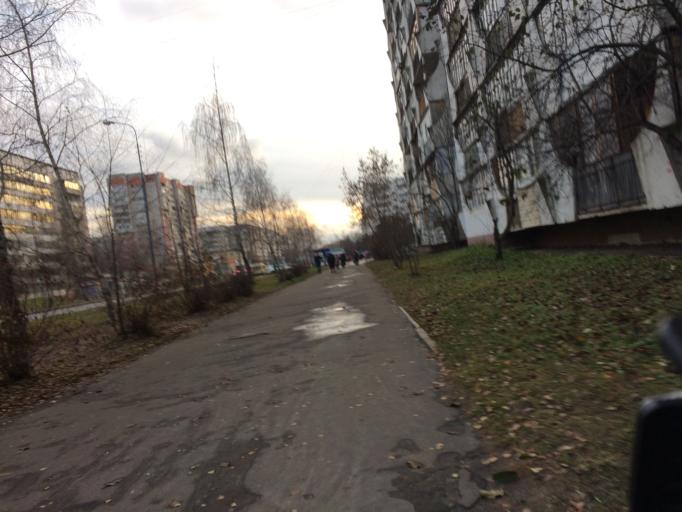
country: RU
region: Mariy-El
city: Yoshkar-Ola
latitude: 56.6324
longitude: 47.9186
